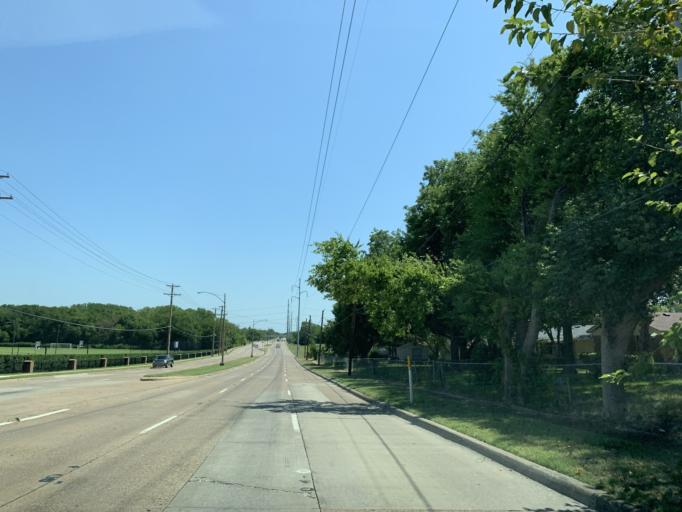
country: US
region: Texas
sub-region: Dallas County
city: Hutchins
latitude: 32.6779
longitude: -96.7521
